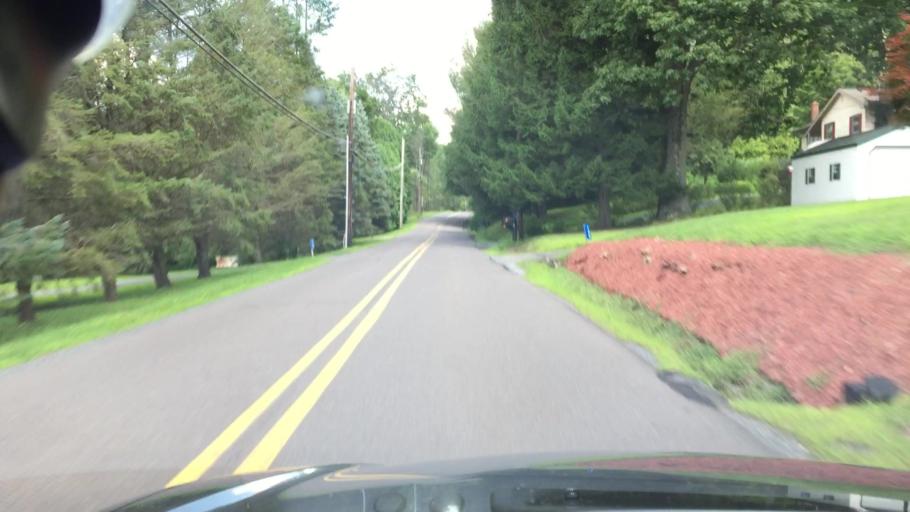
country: US
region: Pennsylvania
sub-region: Luzerne County
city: Harleigh
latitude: 41.0103
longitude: -75.9562
